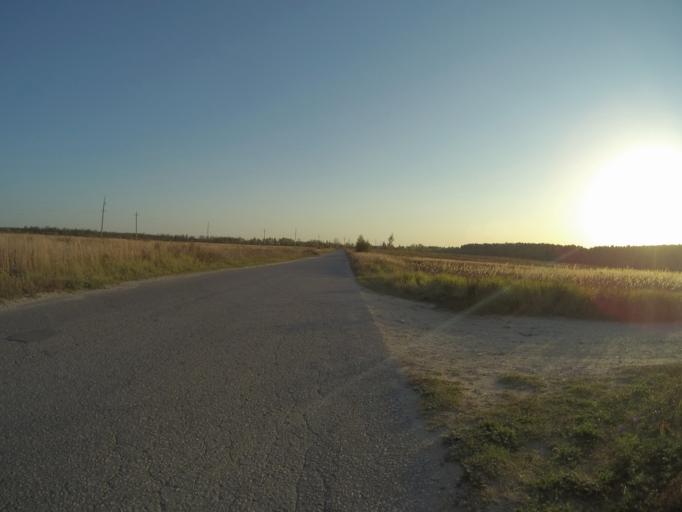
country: RU
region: Vladimir
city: Golovino
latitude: 55.9626
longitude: 40.4552
